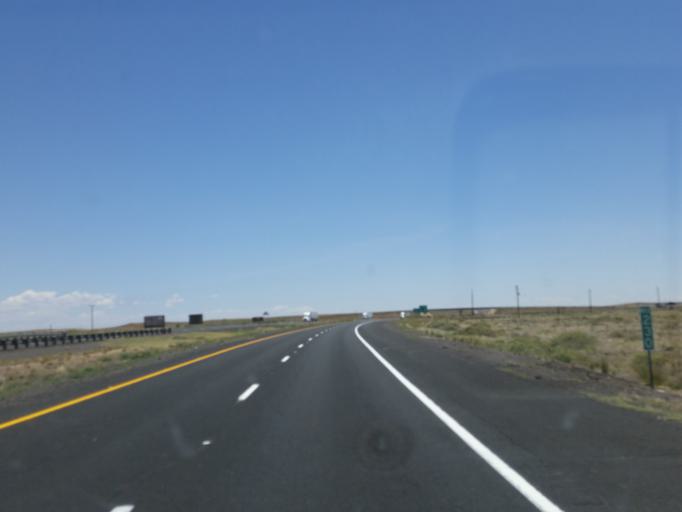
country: US
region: Arizona
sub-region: Coconino County
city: LeChee
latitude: 35.1175
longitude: -111.0990
